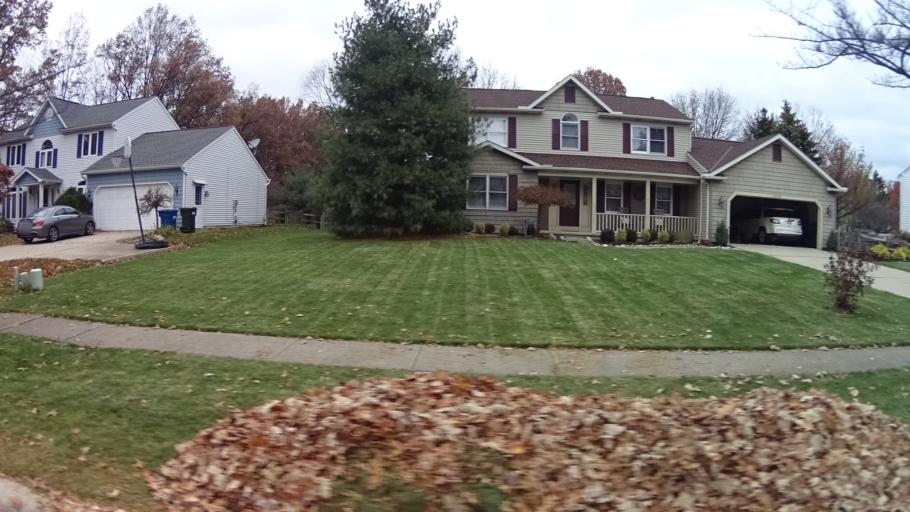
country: US
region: Ohio
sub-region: Lorain County
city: Avon Center
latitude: 41.4861
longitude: -81.9926
